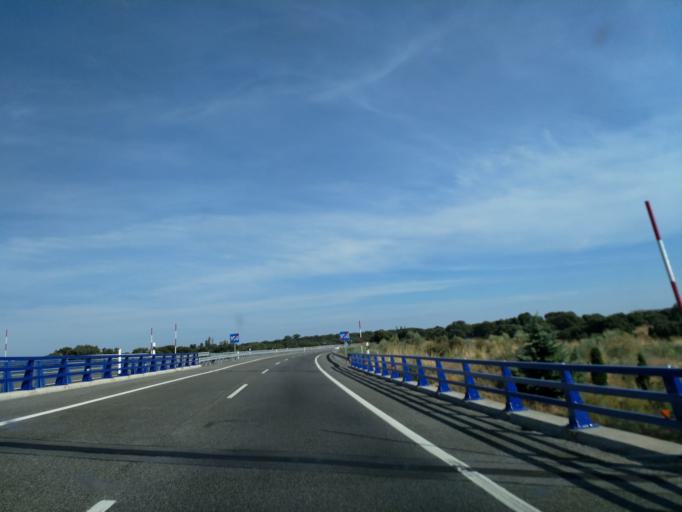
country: ES
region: Castille and Leon
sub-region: Provincia de Avila
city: Avila
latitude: 40.6771
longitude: -4.6864
